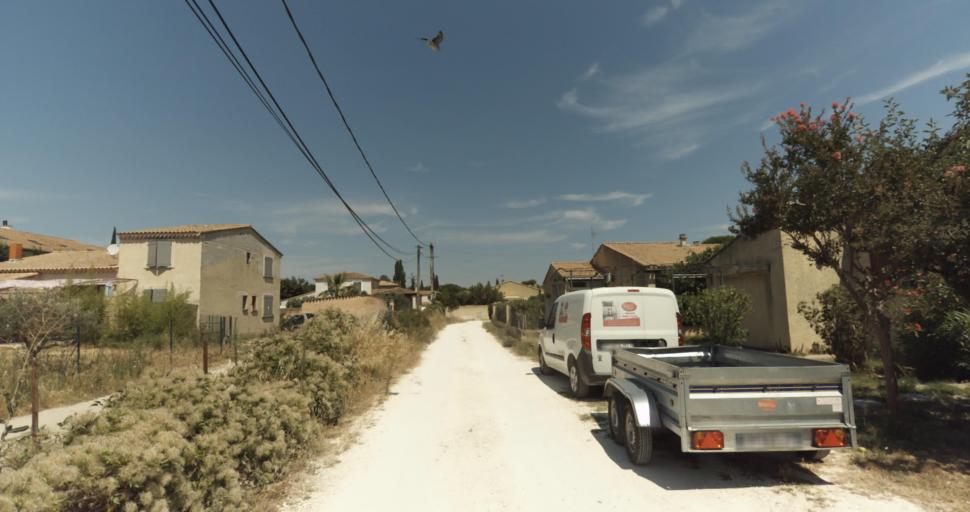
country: FR
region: Provence-Alpes-Cote d'Azur
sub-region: Departement du Vaucluse
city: Monteux
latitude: 44.0305
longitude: 4.9880
